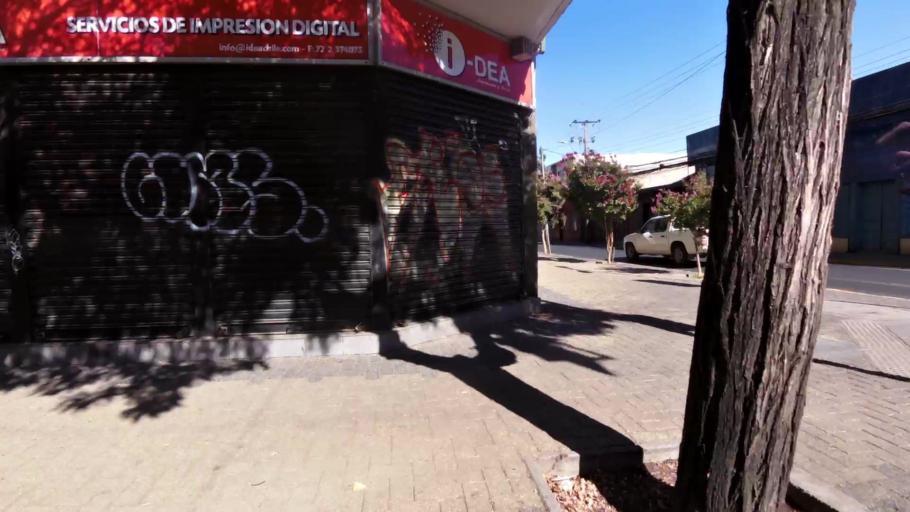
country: CL
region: O'Higgins
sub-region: Provincia de Cachapoal
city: Rancagua
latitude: -34.1695
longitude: -70.7379
